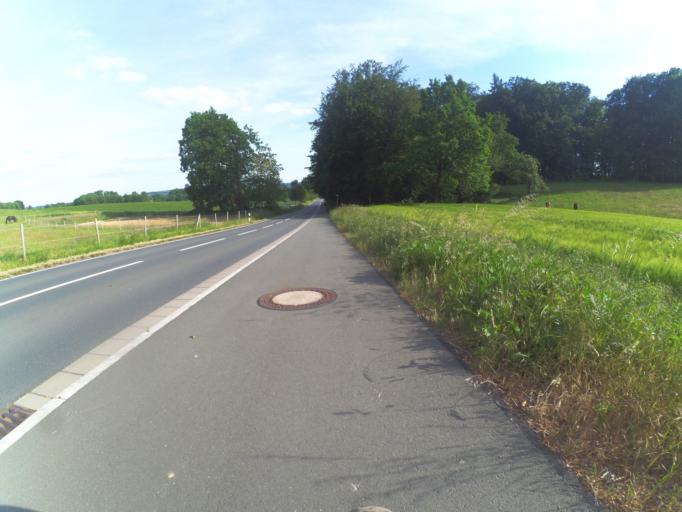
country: DE
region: North Rhine-Westphalia
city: Ibbenburen
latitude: 52.2774
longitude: 7.7473
